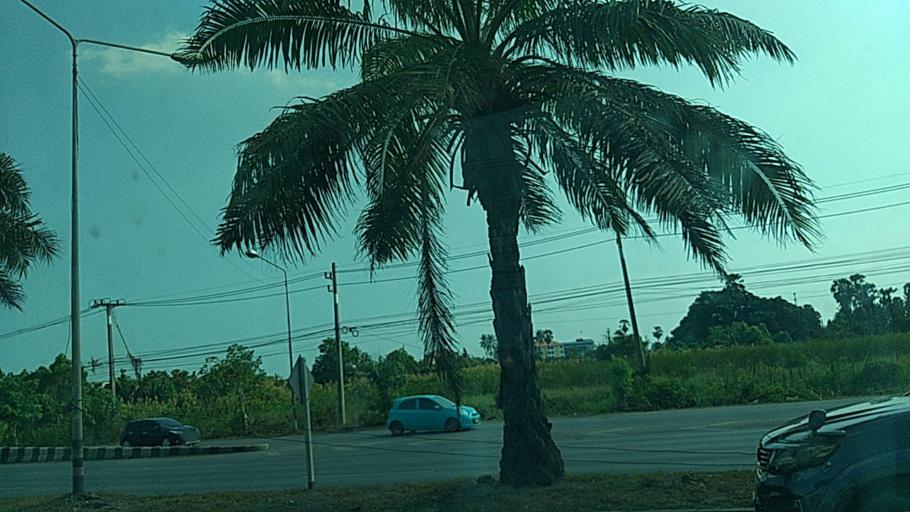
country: TH
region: Pathum Thani
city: Pathum Thani
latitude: 14.0288
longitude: 100.5361
